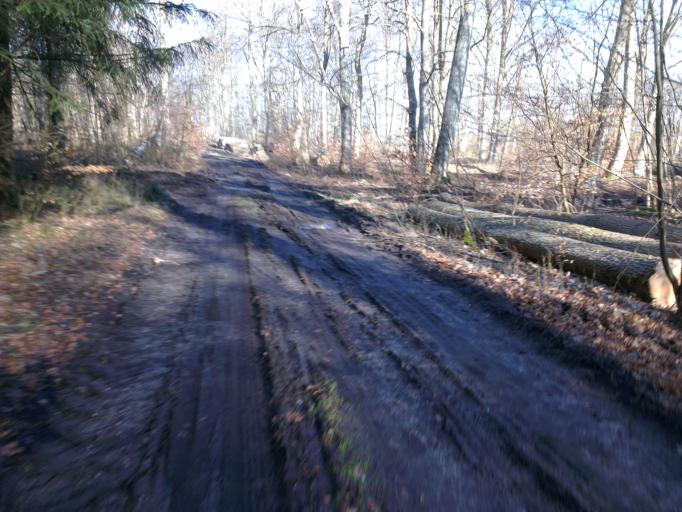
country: DK
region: Capital Region
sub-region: Halsnaes Kommune
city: Frederiksvaerk
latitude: 55.9098
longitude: 12.0077
